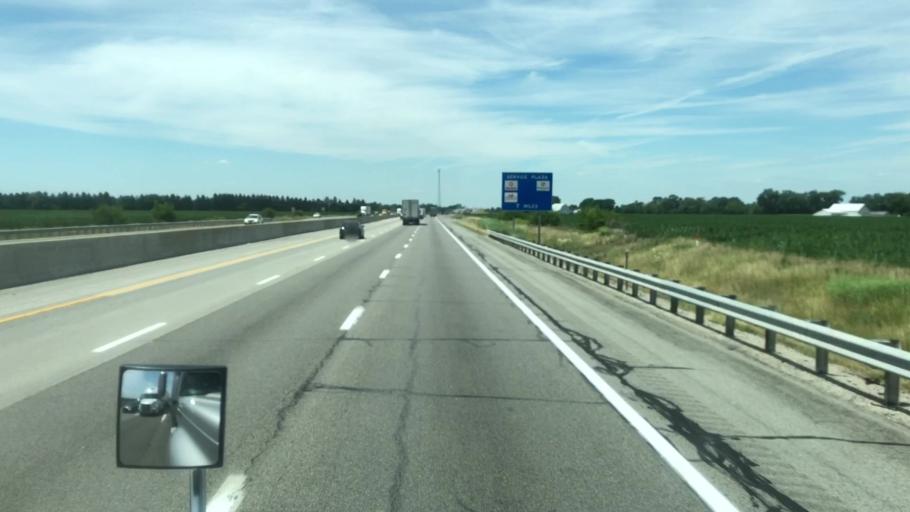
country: US
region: Ohio
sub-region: Ottawa County
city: Elmore
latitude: 41.4423
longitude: -83.2428
